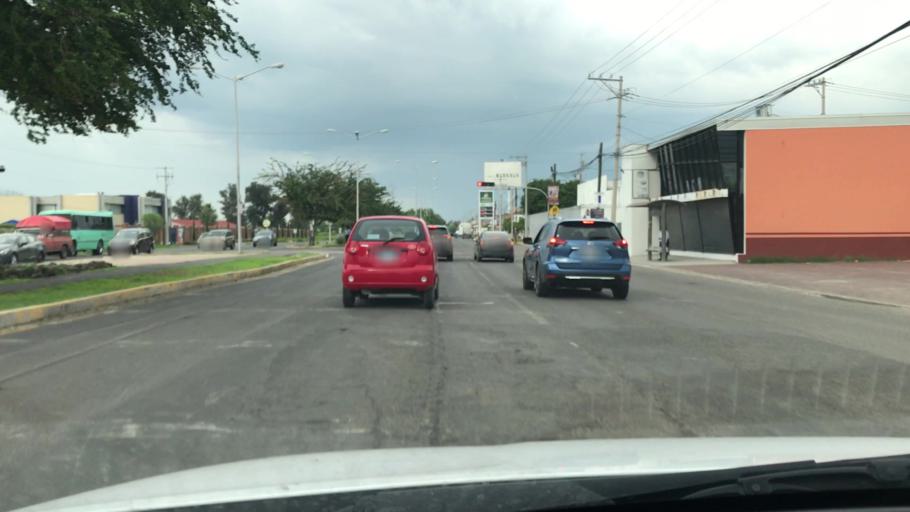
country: MX
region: Guanajuato
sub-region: Celaya
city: La Trinidad
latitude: 20.5364
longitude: -100.7865
